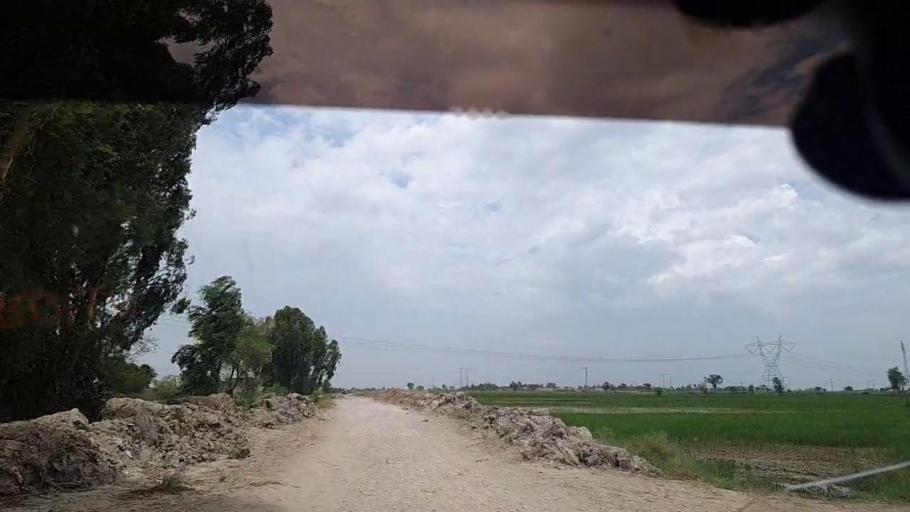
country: PK
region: Sindh
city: Ghauspur
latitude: 28.1082
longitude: 68.9861
